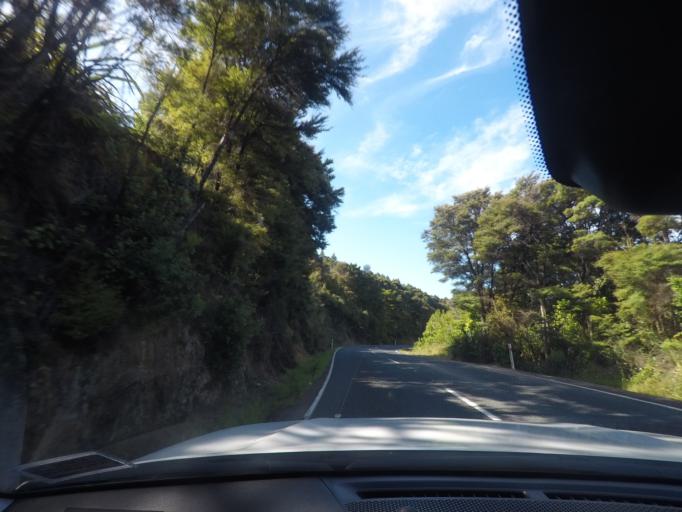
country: NZ
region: Northland
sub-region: Whangarei
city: Ngunguru
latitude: -35.6686
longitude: 174.4700
